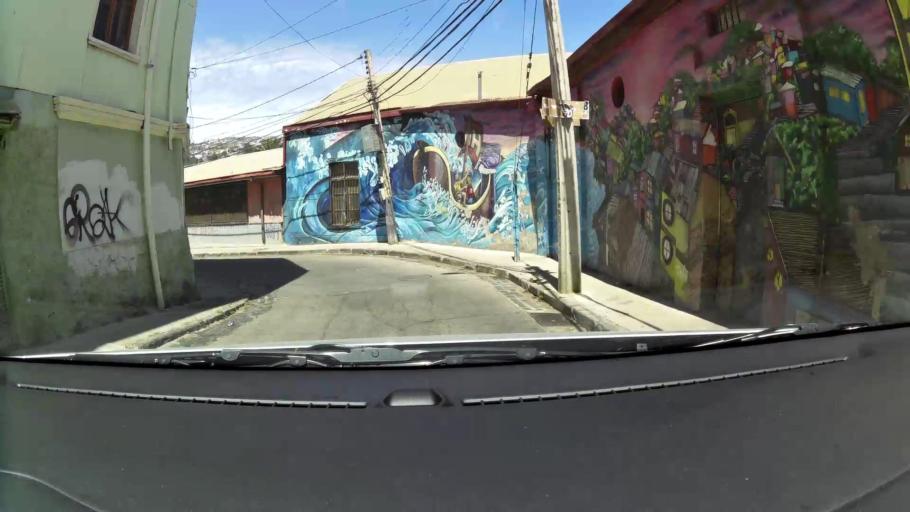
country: CL
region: Valparaiso
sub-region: Provincia de Valparaiso
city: Valparaiso
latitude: -33.0501
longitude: -71.6008
